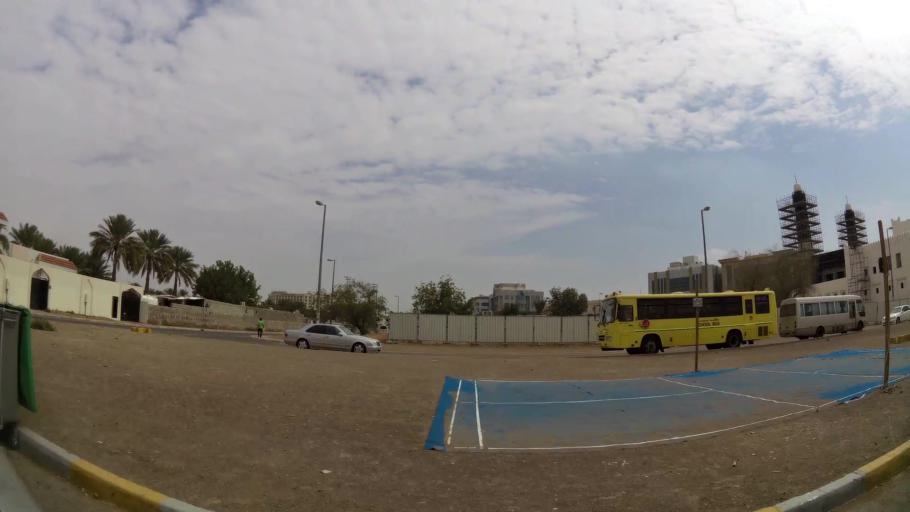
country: OM
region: Al Buraimi
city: Al Buraymi
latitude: 24.2233
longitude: 55.7779
